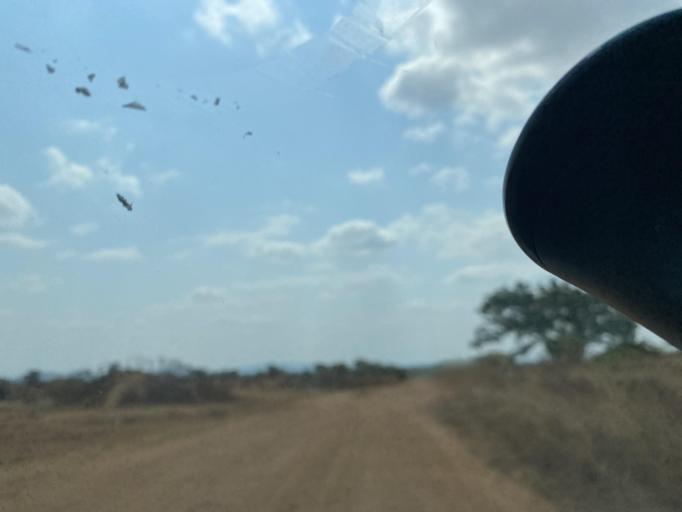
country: ZM
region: Lusaka
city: Chongwe
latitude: -15.5888
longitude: 28.7715
